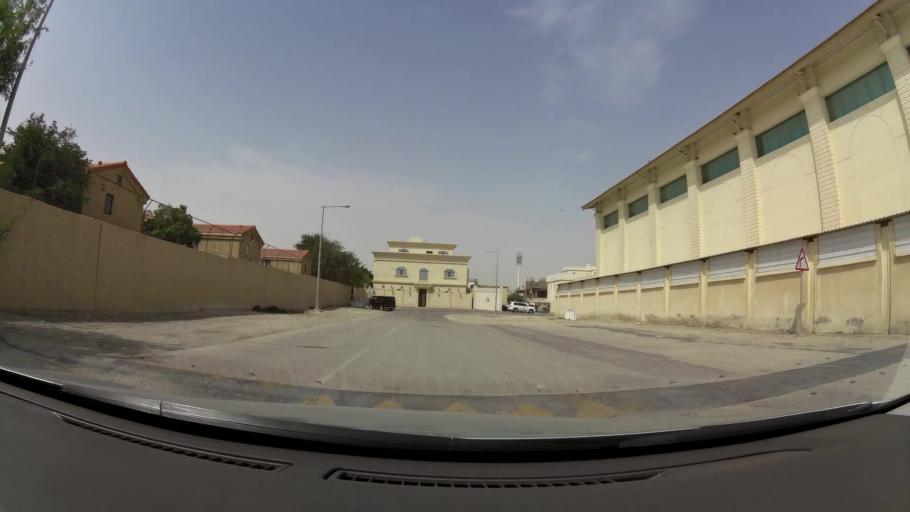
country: QA
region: Baladiyat ad Dawhah
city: Doha
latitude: 25.2997
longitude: 51.4838
